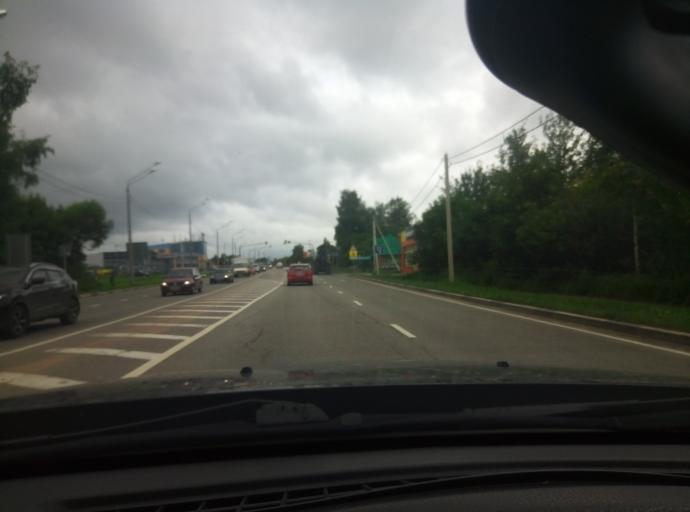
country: RU
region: Moskovskaya
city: Serpukhov
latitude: 54.9115
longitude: 37.4841
